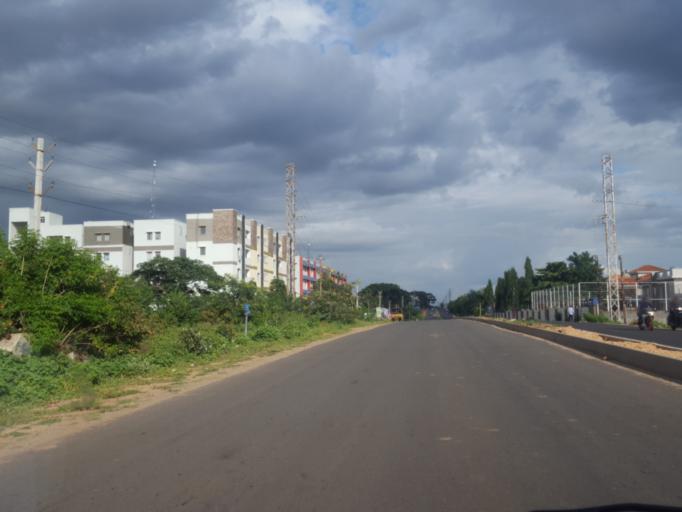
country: IN
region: Telangana
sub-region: Rangareddi
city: Singapur
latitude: 17.4249
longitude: 78.2050
